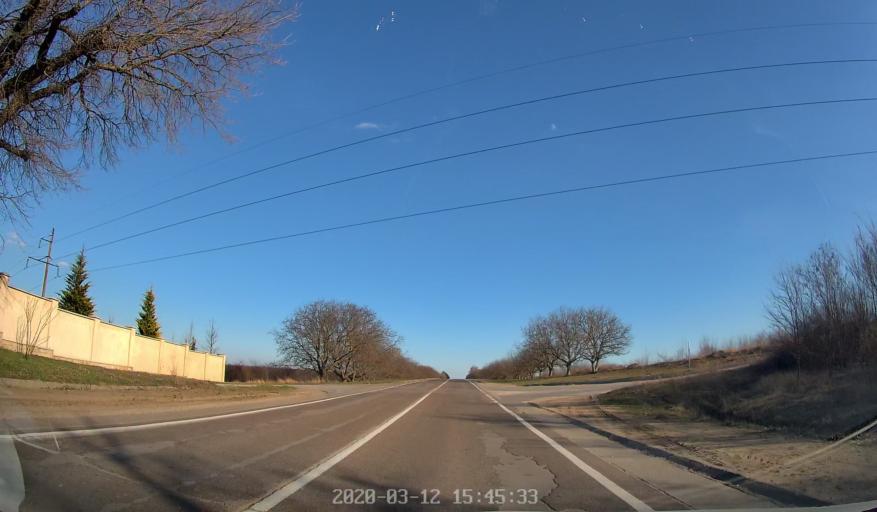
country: MD
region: Chisinau
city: Stauceni
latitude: 47.1052
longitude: 28.8773
